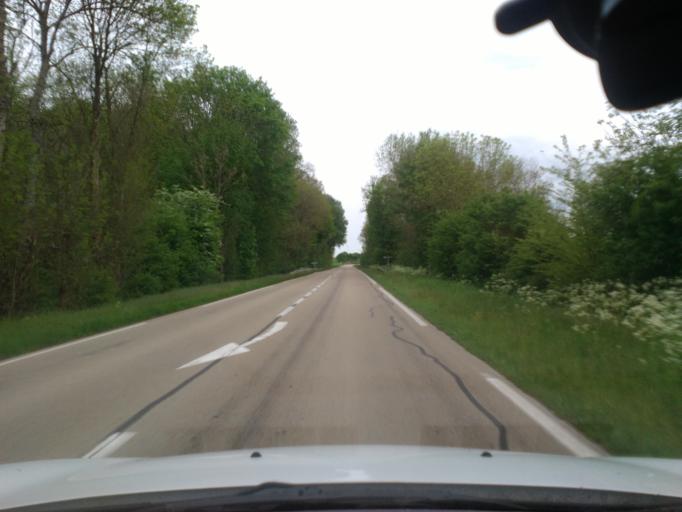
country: FR
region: Champagne-Ardenne
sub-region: Departement de la Haute-Marne
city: Lavilleneuve-au-Roi
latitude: 48.1807
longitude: 4.9842
